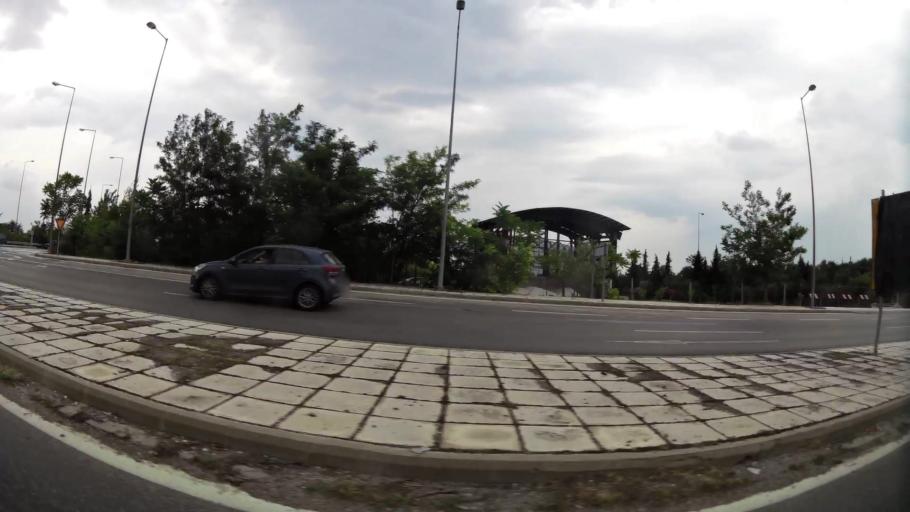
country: GR
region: Central Macedonia
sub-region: Nomos Imathias
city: Veroia
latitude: 40.5061
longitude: 22.2286
